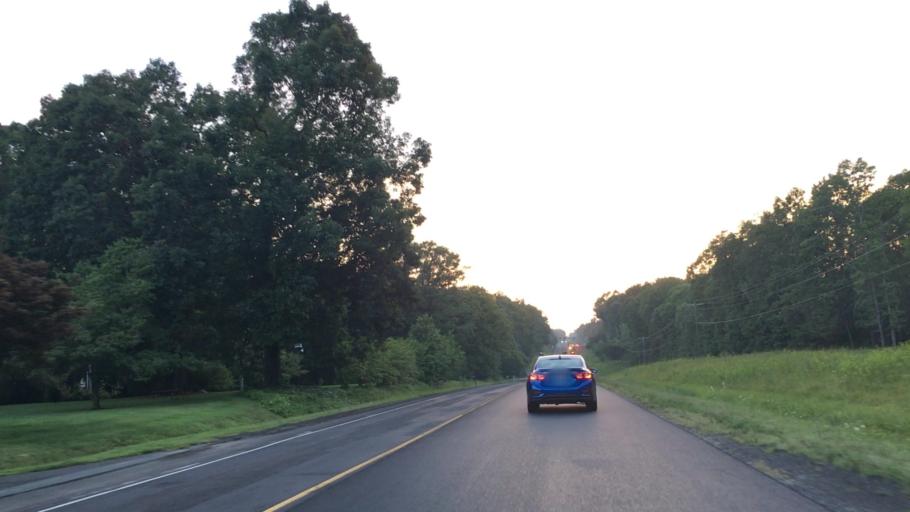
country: US
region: Virginia
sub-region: Spotsylvania County
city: Spotsylvania
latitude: 38.3136
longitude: -77.7721
